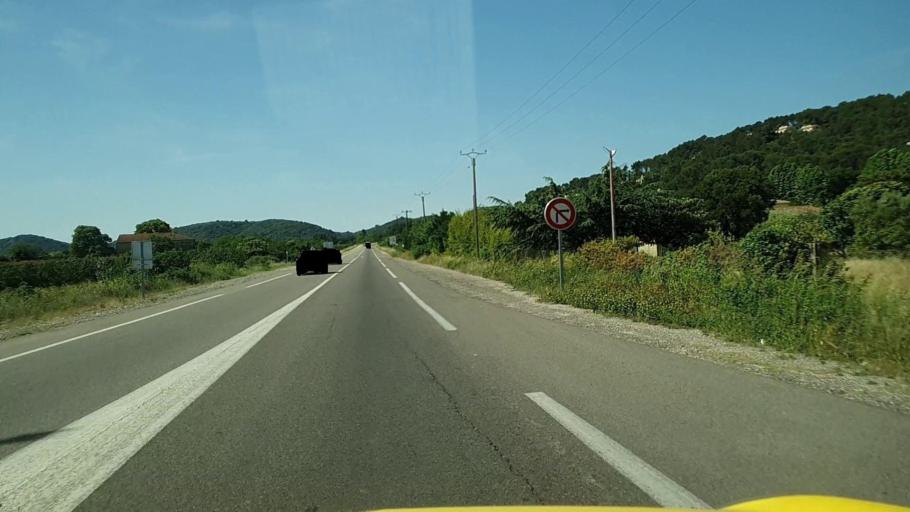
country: FR
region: Languedoc-Roussillon
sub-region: Departement du Gard
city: Connaux
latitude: 44.0871
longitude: 4.5949
